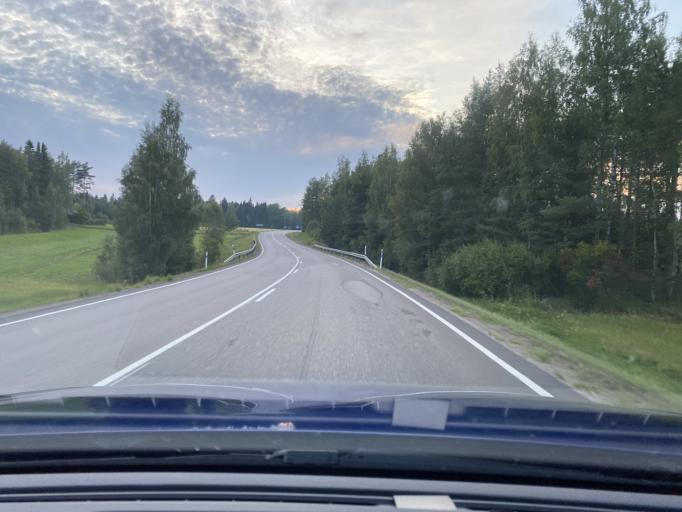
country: FI
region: Satakunta
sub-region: Pohjois-Satakunta
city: Honkajoki
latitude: 61.9202
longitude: 22.2569
